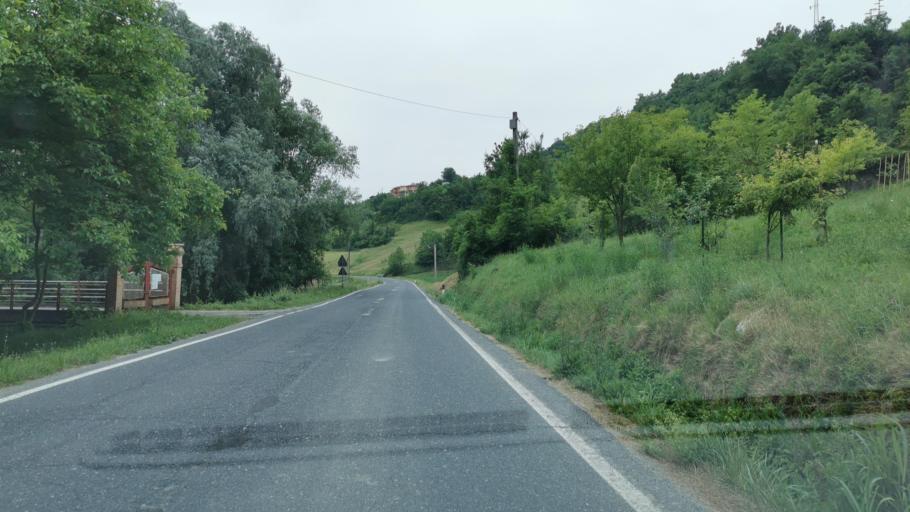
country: IT
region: Piedmont
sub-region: Provincia di Cuneo
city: Ceva
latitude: 44.3935
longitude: 8.0470
